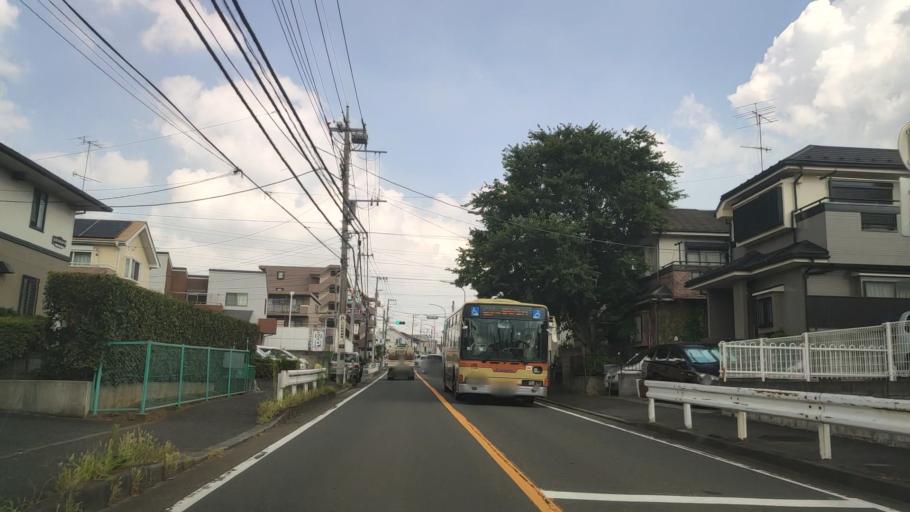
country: JP
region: Kanagawa
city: Minami-rinkan
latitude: 35.4500
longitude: 139.5033
